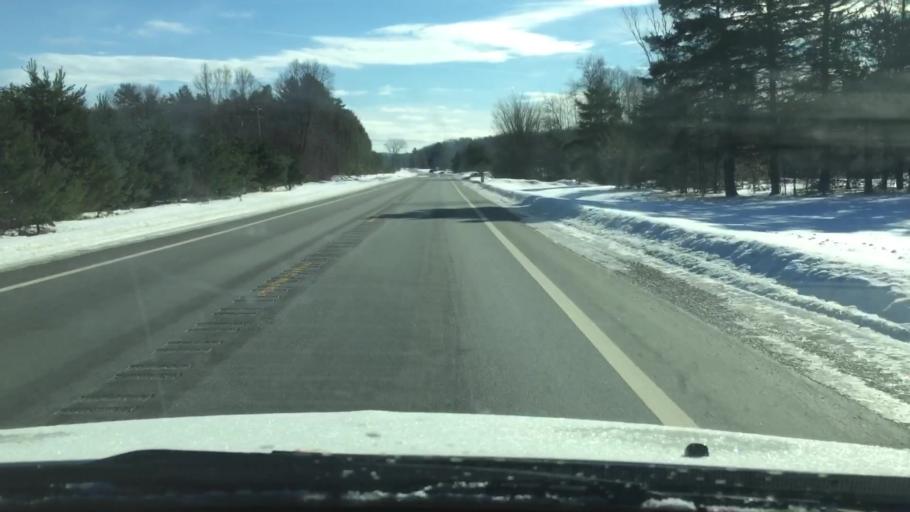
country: US
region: Michigan
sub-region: Charlevoix County
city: East Jordan
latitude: 45.0777
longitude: -85.0882
